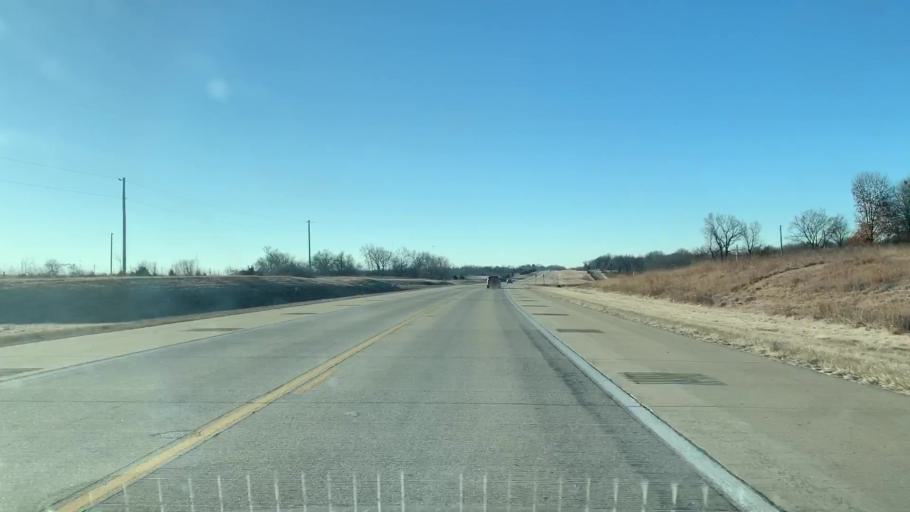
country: US
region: Kansas
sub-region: Crawford County
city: Arma
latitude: 37.5737
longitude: -94.7048
